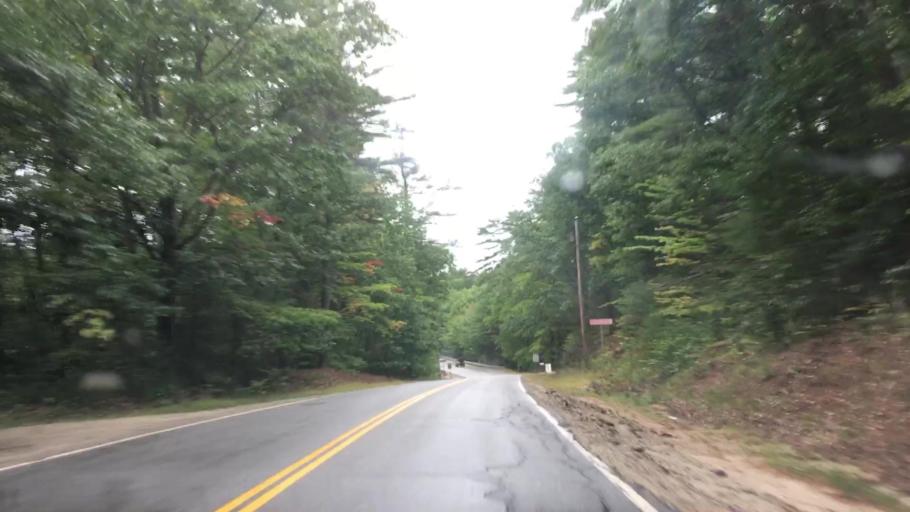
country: US
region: Maine
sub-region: Cumberland County
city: Raymond
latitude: 43.9481
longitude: -70.4626
